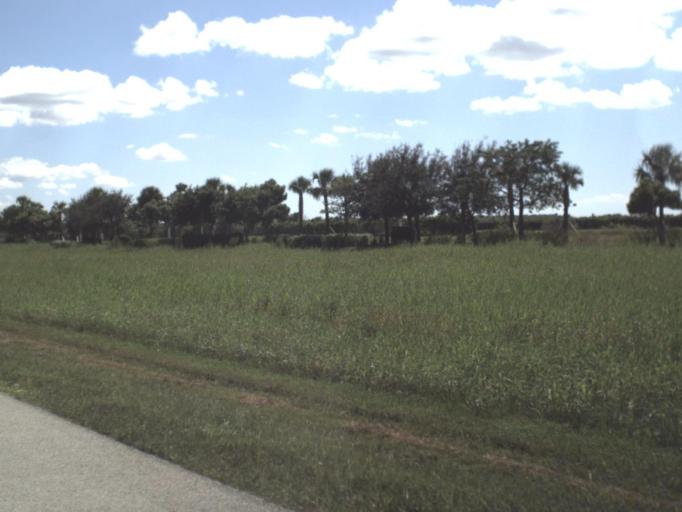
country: US
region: Florida
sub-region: Collier County
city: Lely Resort
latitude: 26.0150
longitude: -81.6237
